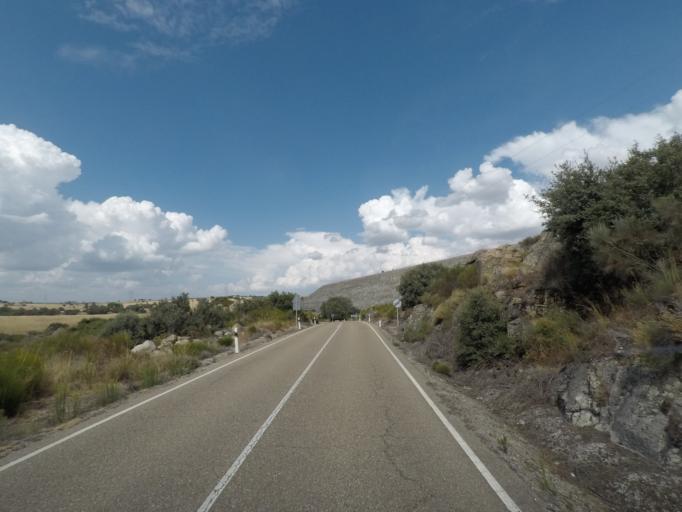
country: ES
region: Castille and Leon
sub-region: Provincia de Salamanca
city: Almendra
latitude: 41.2840
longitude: -6.3337
